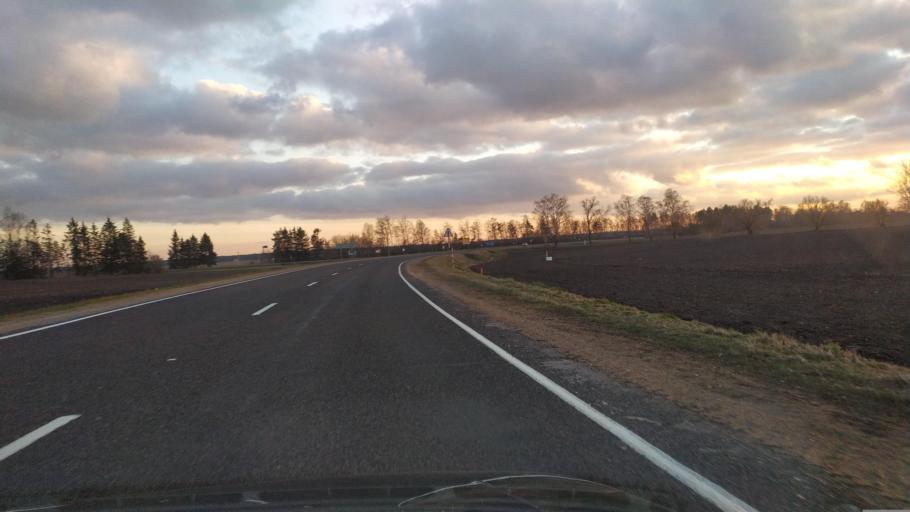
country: BY
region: Brest
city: Kamyanyets
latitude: 52.3731
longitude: 23.7924
